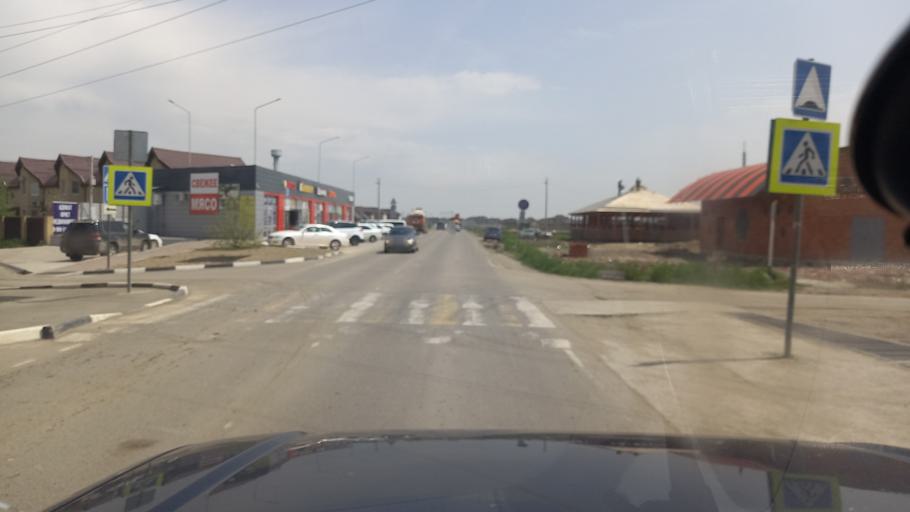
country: RU
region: Adygeya
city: Yablonovskiy
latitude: 44.9857
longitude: 38.9663
